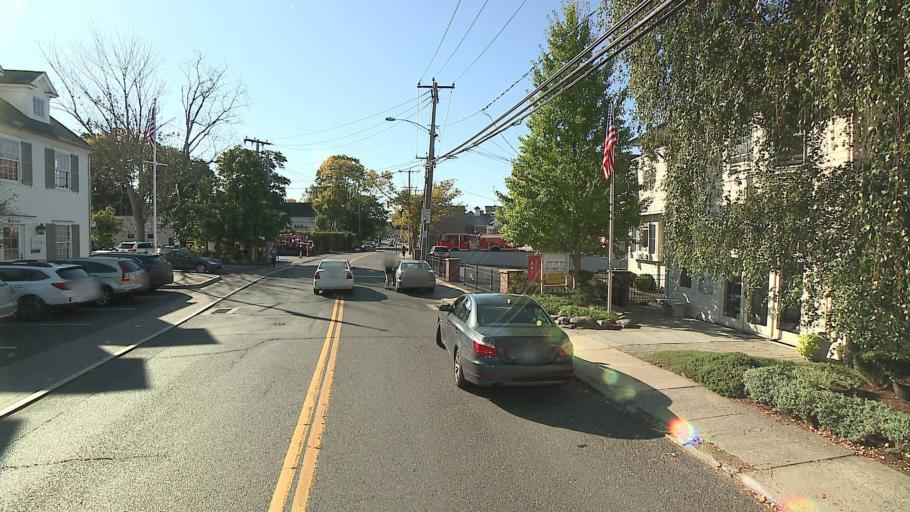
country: US
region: Connecticut
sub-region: Fairfield County
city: Darien
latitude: 41.0680
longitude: -73.4436
